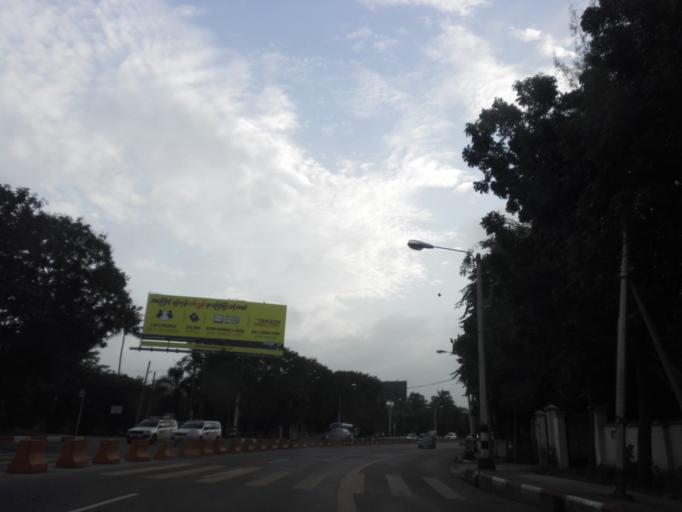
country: MM
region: Yangon
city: Yangon
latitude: 16.8478
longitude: 96.1365
